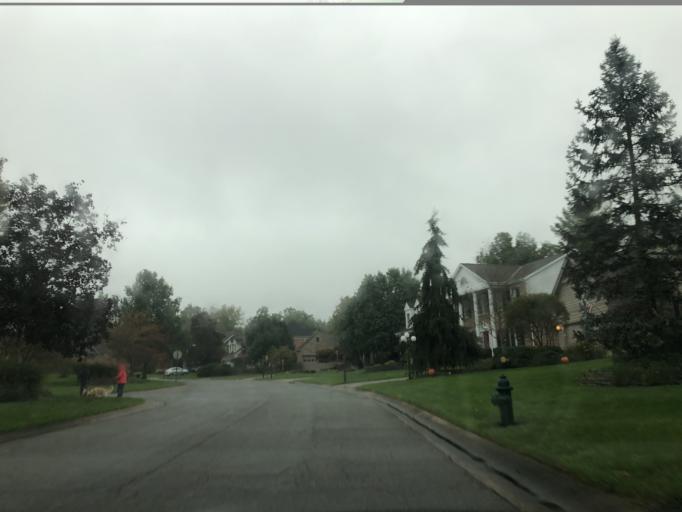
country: US
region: Ohio
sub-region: Hamilton County
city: The Village of Indian Hill
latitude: 39.2674
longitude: -84.2864
